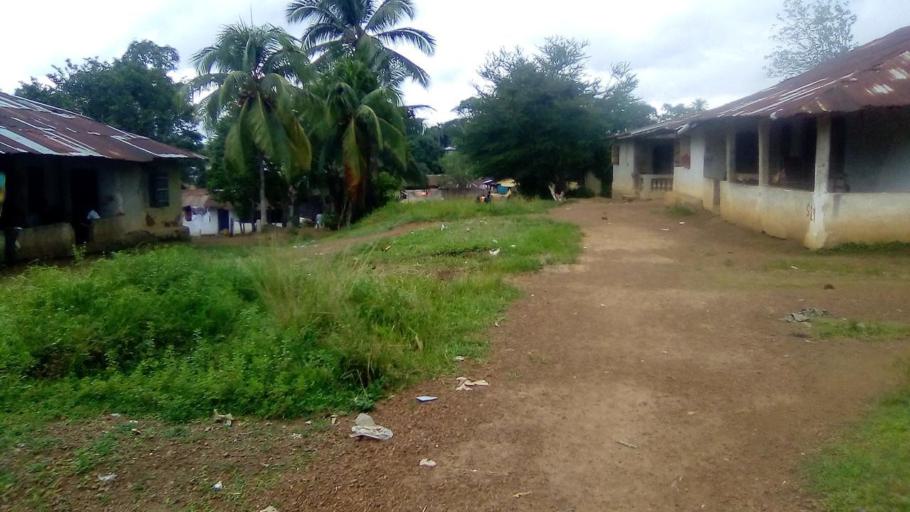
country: SL
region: Southern Province
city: Pujehun
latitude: 7.3602
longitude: -11.7249
